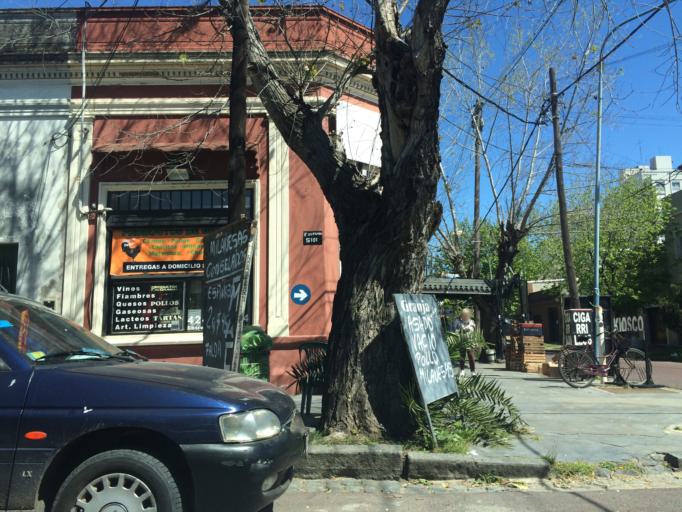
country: AR
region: Buenos Aires
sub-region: Partido de Lomas de Zamora
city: Lomas de Zamora
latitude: -34.7334
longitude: -58.3957
